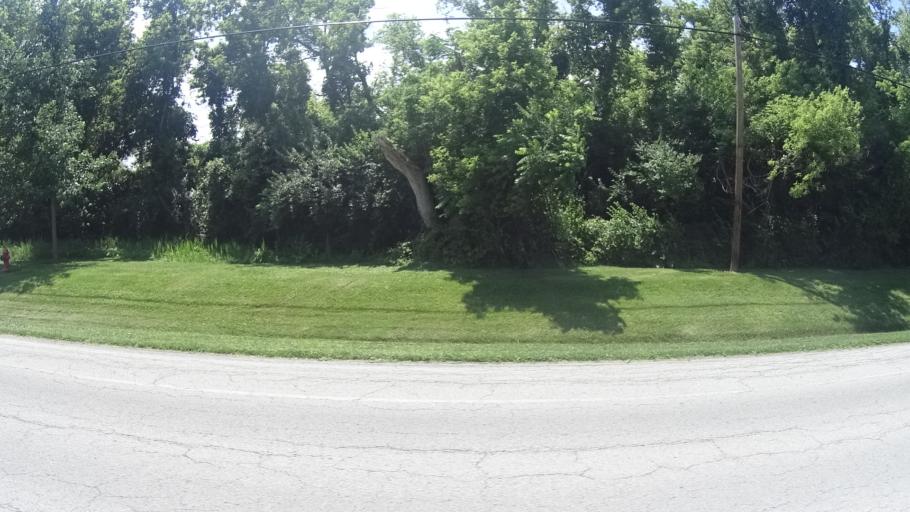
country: US
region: Ohio
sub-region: Erie County
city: Huron
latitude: 41.3766
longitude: -82.5463
